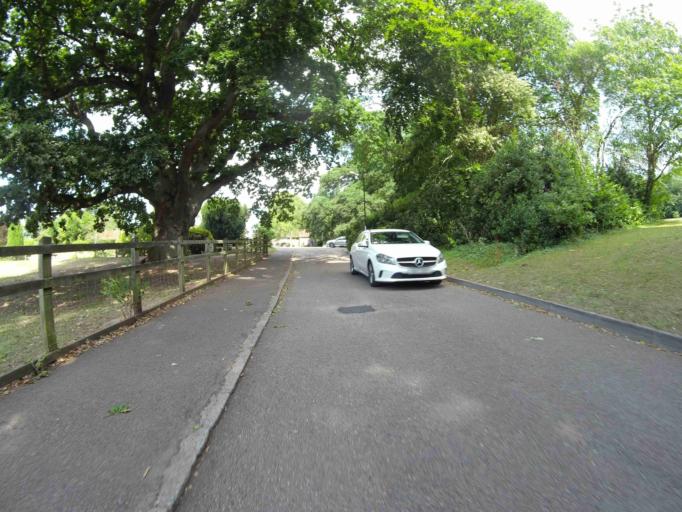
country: GB
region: England
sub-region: Devon
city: Exmouth
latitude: 50.6244
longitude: -3.4023
